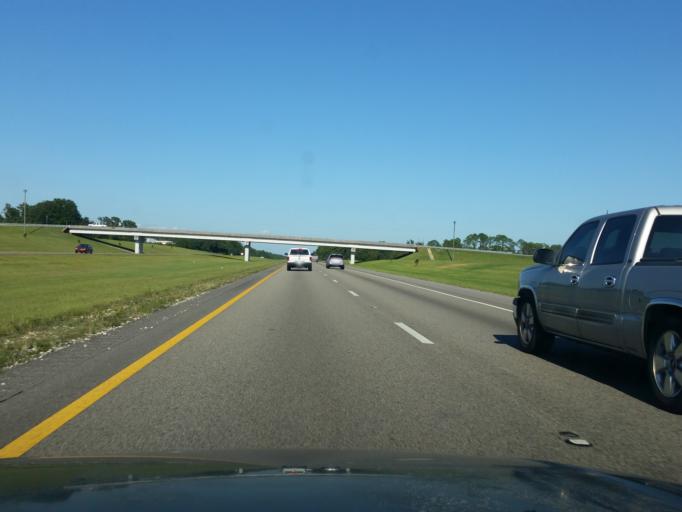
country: US
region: Mississippi
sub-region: Hancock County
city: Diamondhead
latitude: 30.3717
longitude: -89.3793
